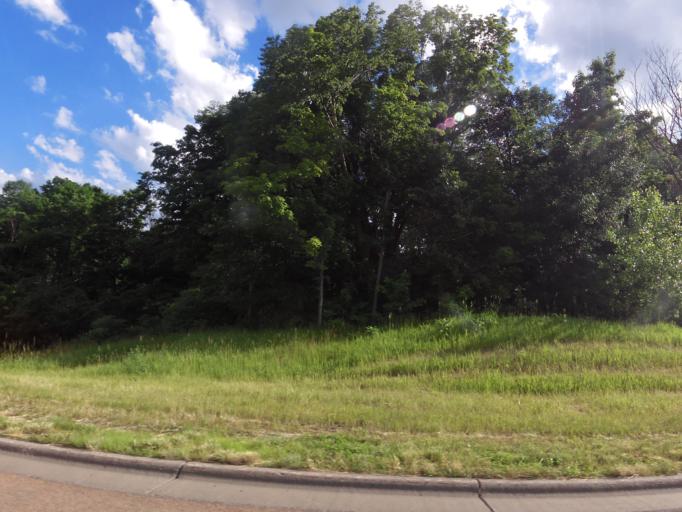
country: US
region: Minnesota
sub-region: Carver County
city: Waconia
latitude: 44.8361
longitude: -93.7706
